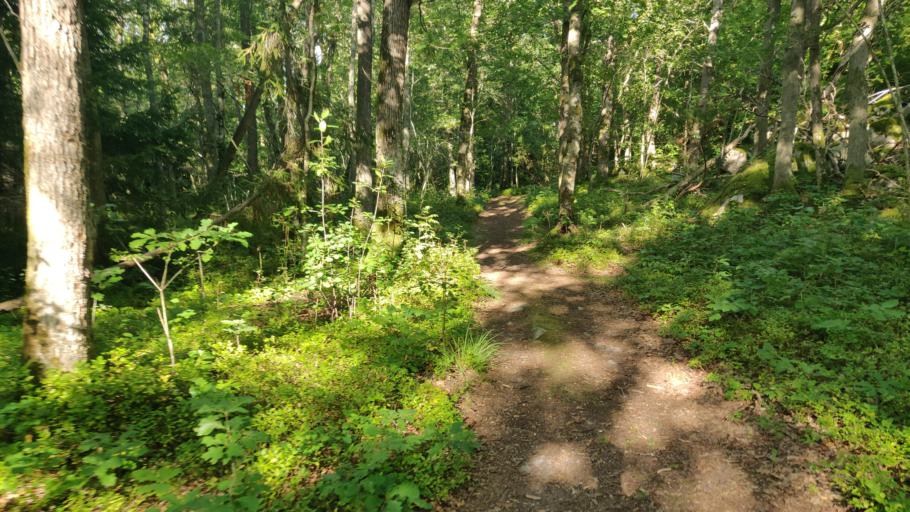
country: SE
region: Vaestra Goetaland
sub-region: Goteborg
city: Torslanda
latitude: 57.7861
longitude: 11.8202
